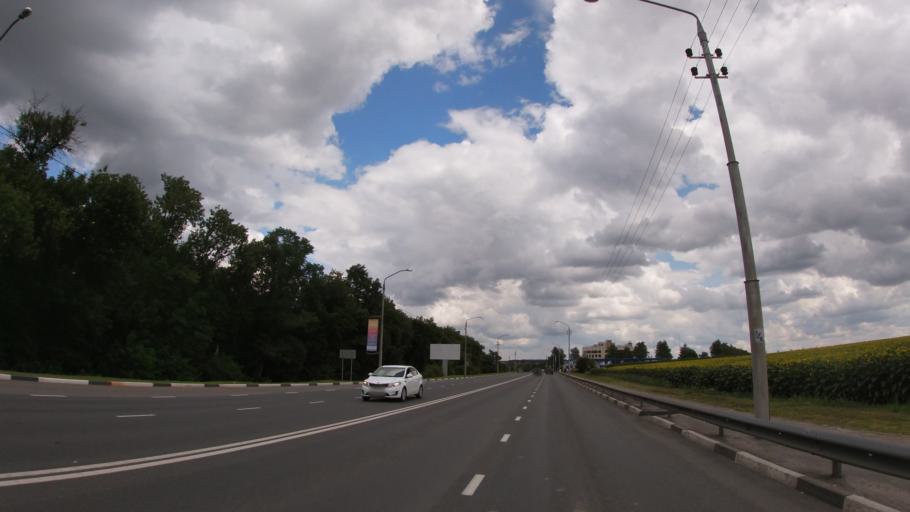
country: RU
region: Belgorod
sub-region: Belgorodskiy Rayon
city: Belgorod
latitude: 50.5523
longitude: 36.5774
